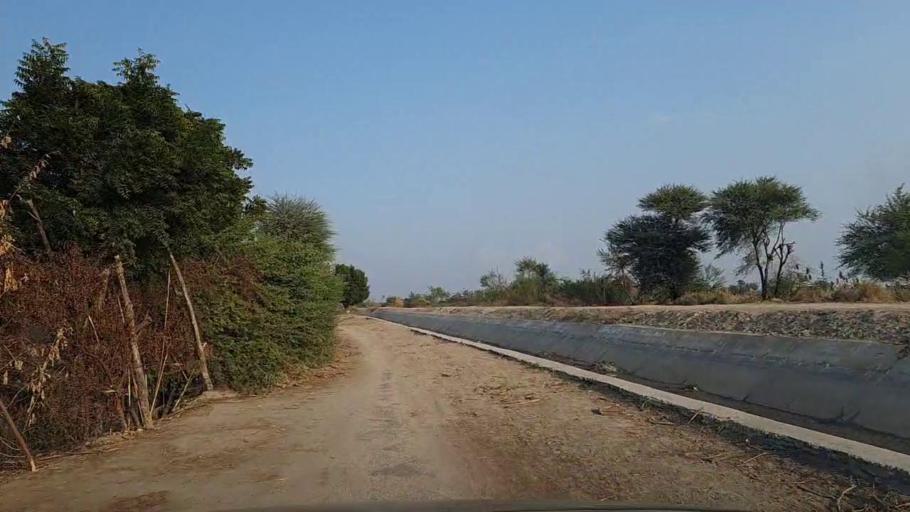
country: PK
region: Sindh
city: Jam Sahib
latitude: 26.3365
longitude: 68.5754
